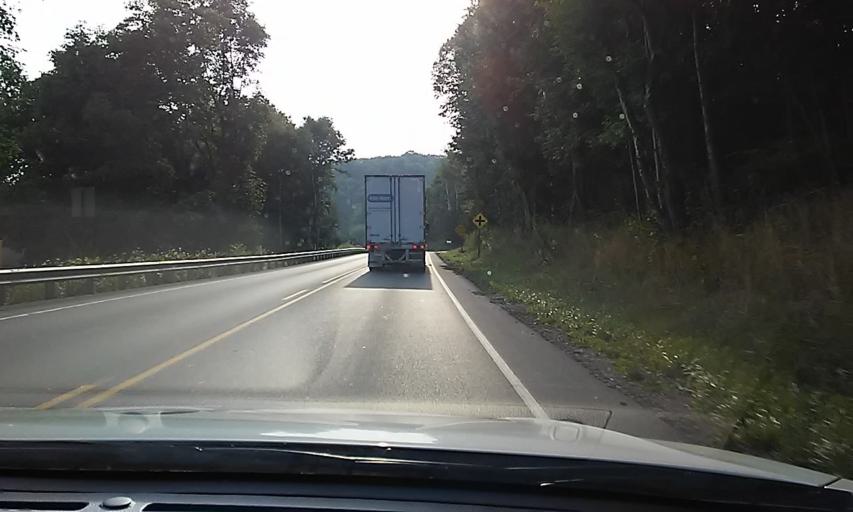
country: US
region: Pennsylvania
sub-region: McKean County
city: Port Allegany
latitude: 41.8283
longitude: -78.3353
